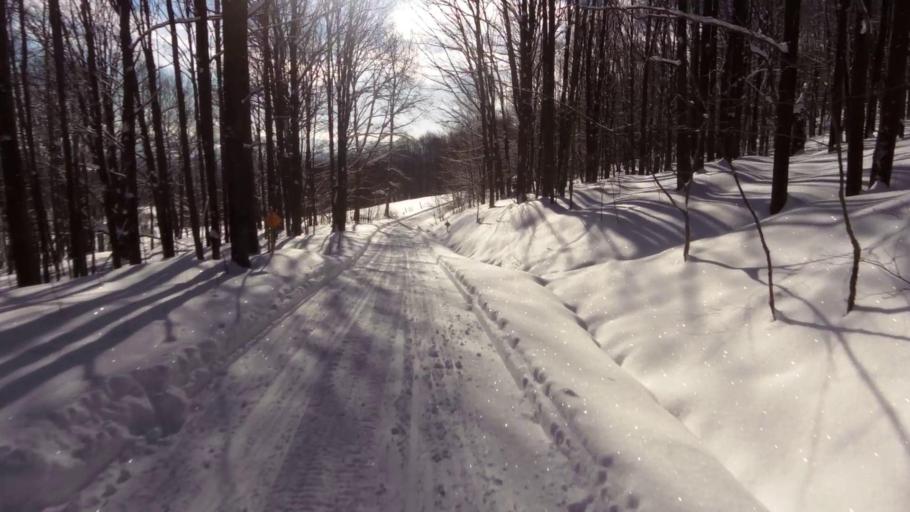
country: US
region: New York
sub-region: Chautauqua County
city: Falconer
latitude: 42.2738
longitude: -79.1213
